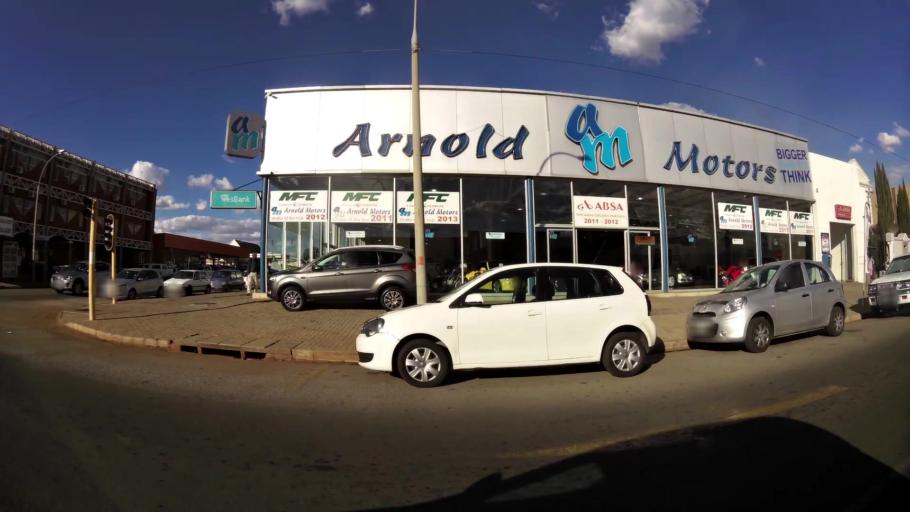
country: ZA
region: North-West
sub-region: Dr Kenneth Kaunda District Municipality
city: Klerksdorp
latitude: -26.8669
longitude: 26.6679
